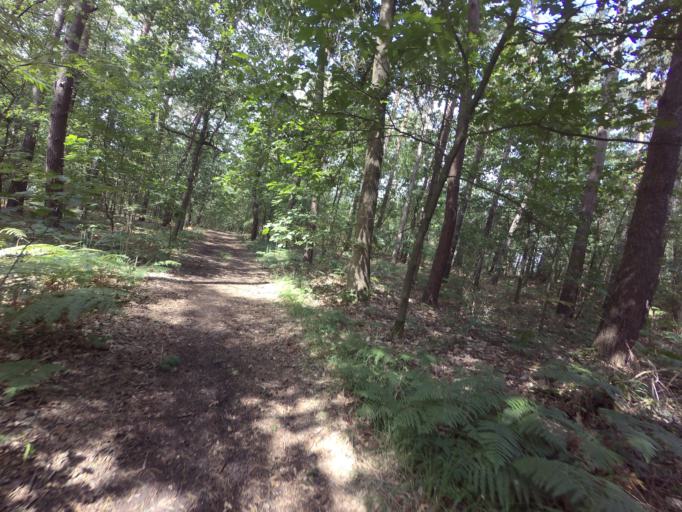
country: NL
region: Limburg
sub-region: Gemeente Heerlen
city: Heerlen
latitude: 50.9173
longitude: 5.9998
